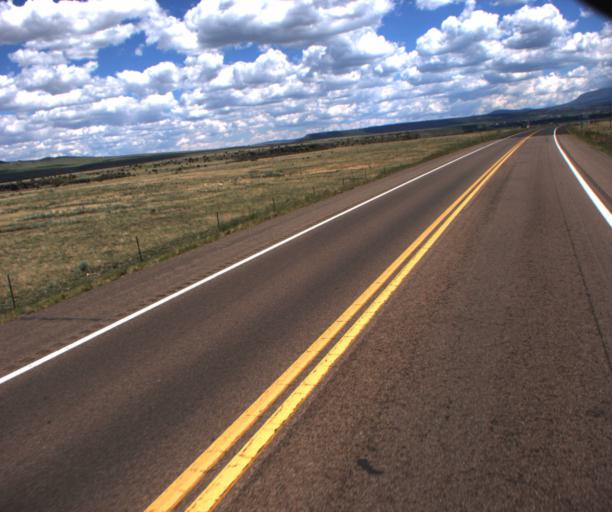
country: US
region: Arizona
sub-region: Apache County
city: Springerville
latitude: 34.1694
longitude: -109.3125
